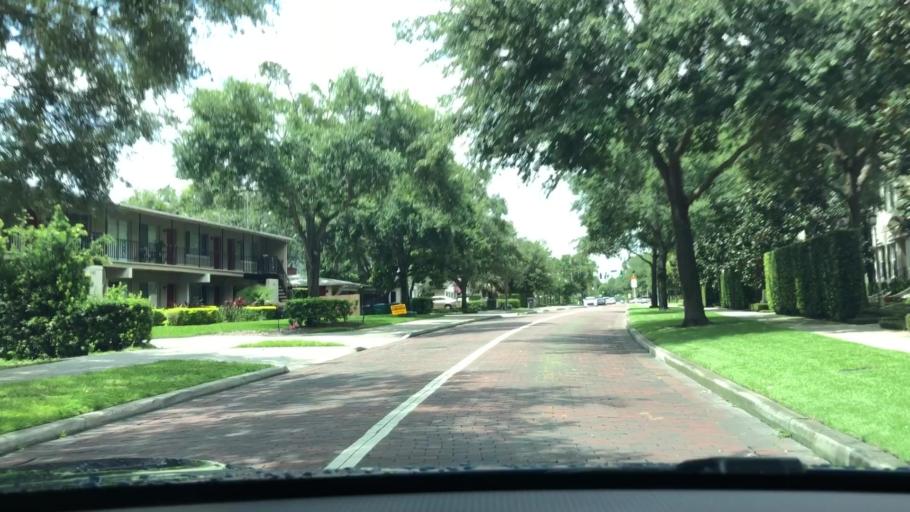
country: US
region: Florida
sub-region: Orange County
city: Winter Park
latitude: 28.5880
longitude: -81.3567
